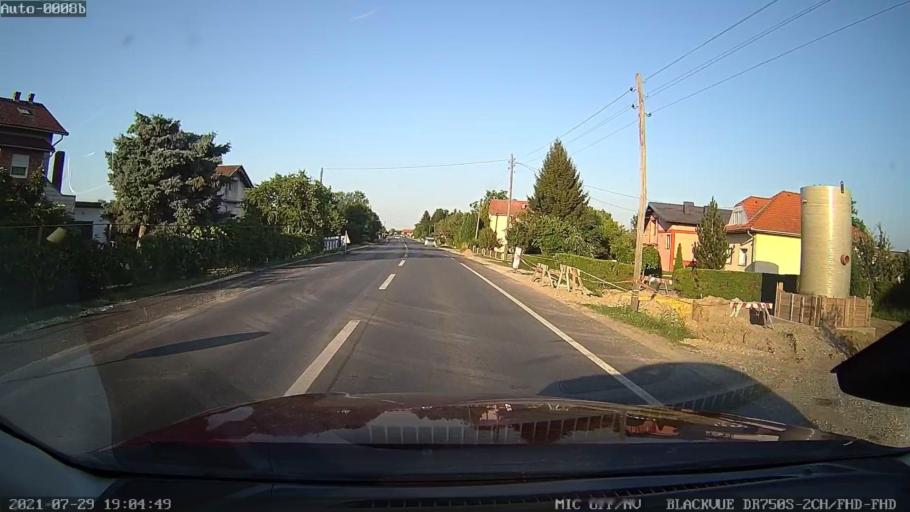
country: HR
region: Medimurska
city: Kursanec
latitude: 46.2975
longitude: 16.4390
